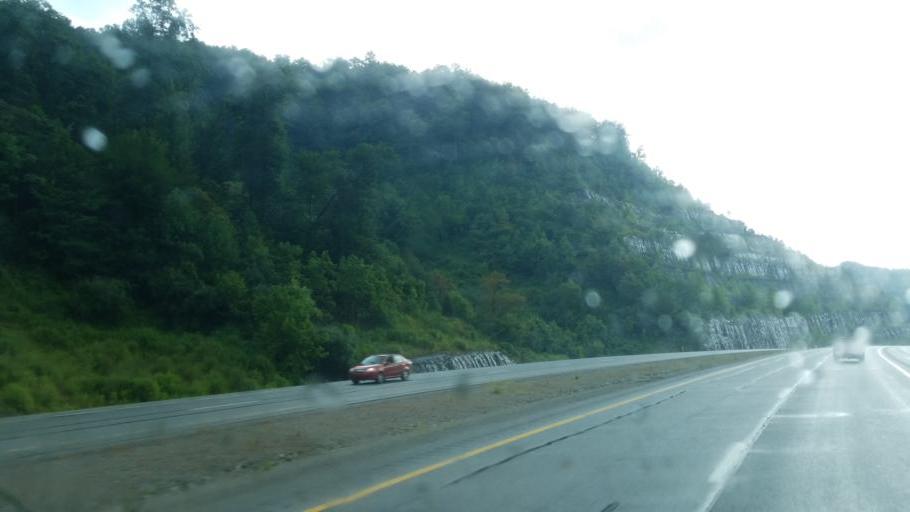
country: US
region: Kentucky
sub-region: Pike County
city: Pikeville
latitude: 37.5312
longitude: -82.4502
